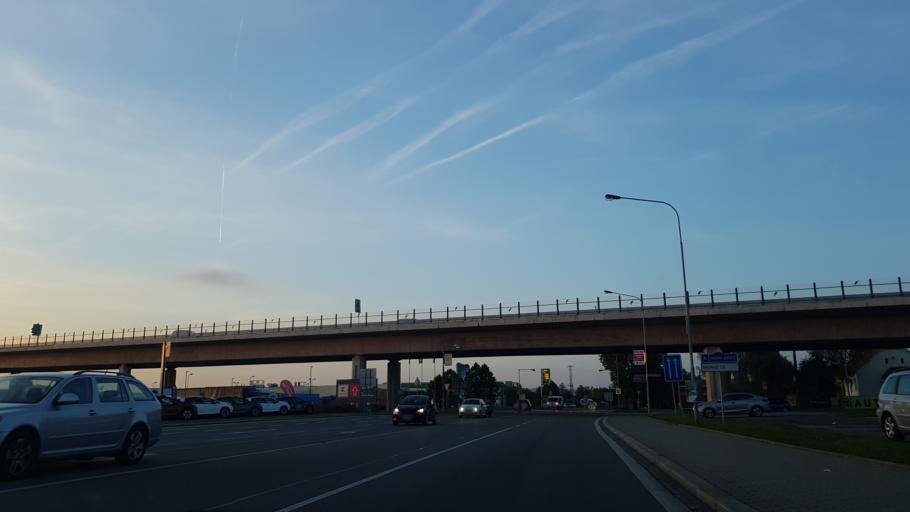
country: CZ
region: Zlin
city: Kunovice
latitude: 49.0490
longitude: 17.4669
